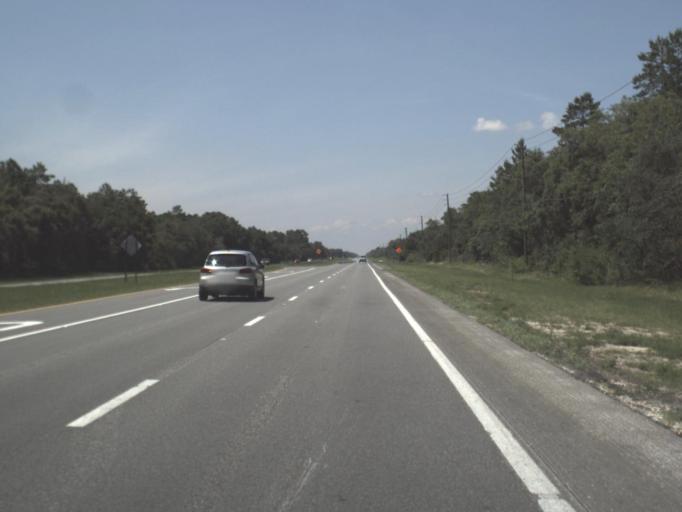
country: US
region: Florida
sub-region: Hernando County
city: North Weeki Wachee
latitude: 28.6104
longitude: -82.5517
